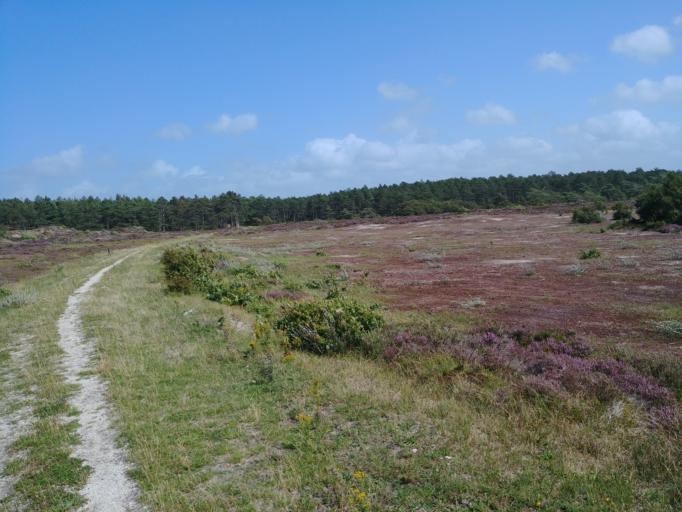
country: NL
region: North Holland
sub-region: Gemeente Bergen
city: Egmond aan Zee
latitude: 52.6914
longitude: 4.6525
